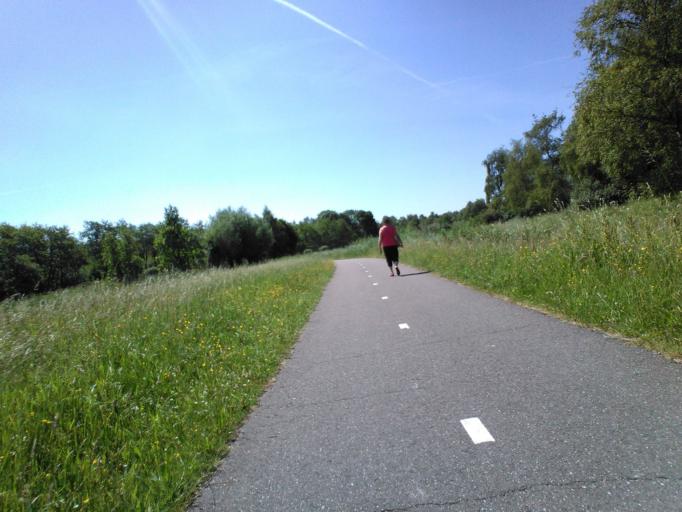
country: NL
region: South Holland
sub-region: Molenwaard
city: Nieuw-Lekkerland
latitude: 51.9294
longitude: 4.6939
